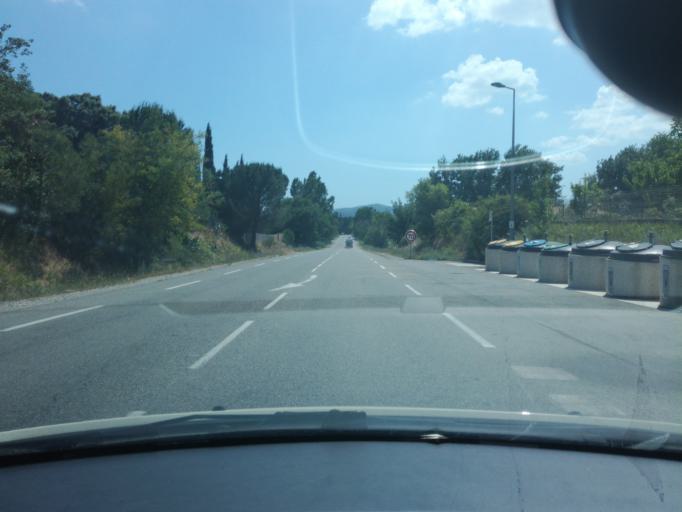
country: FR
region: Provence-Alpes-Cote d'Azur
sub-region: Departement du Var
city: Le Muy
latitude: 43.4847
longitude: 6.5669
